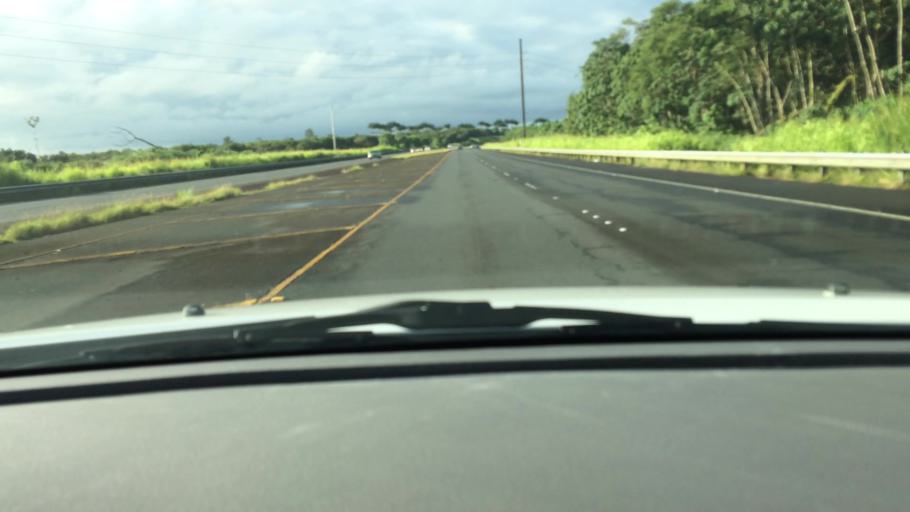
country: US
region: Hawaii
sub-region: Hawaii County
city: Kea'au
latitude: 19.6240
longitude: -155.0320
